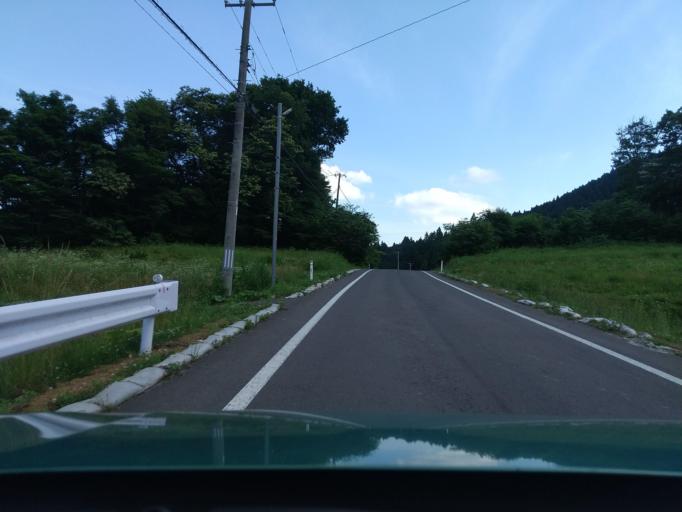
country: JP
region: Iwate
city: Ichinoseki
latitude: 38.9988
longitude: 141.2185
